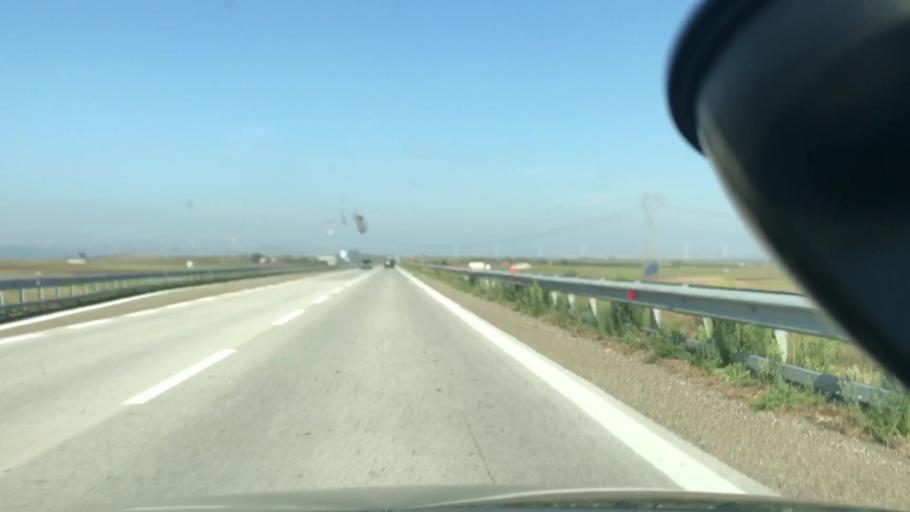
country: IT
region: Basilicate
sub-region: Provincia di Potenza
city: Venosa
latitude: 40.9959
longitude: 15.8813
